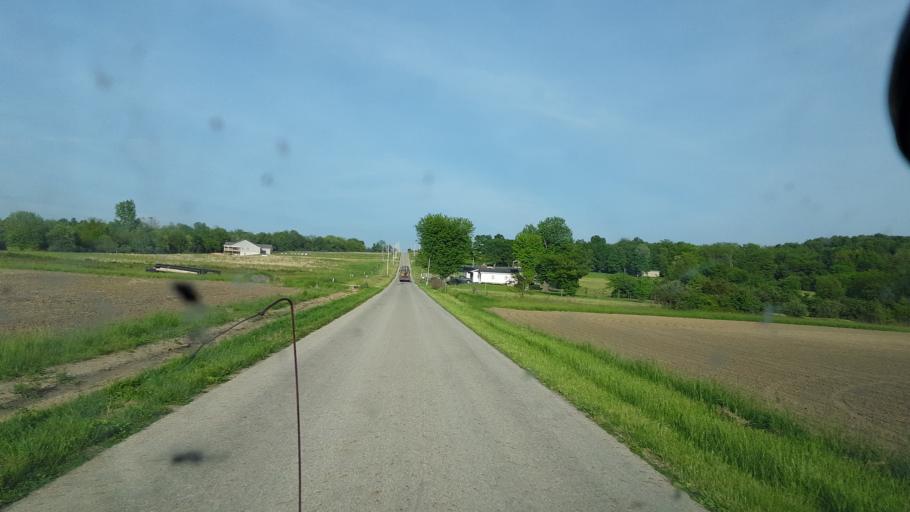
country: US
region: Ohio
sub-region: Ross County
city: Kingston
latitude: 39.5126
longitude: -82.7645
